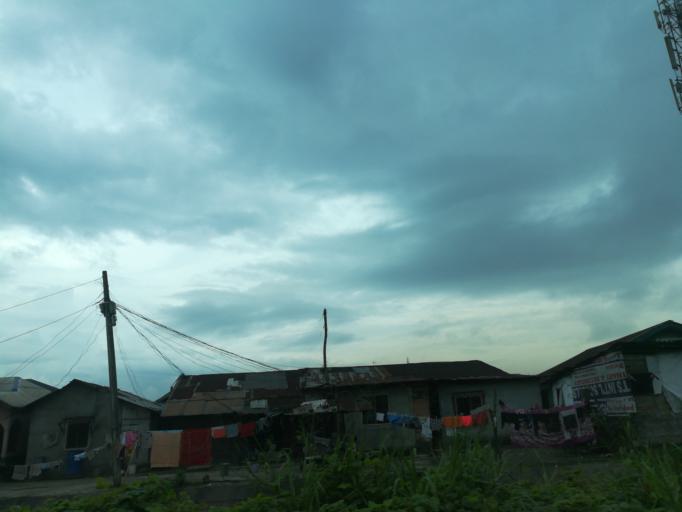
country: NG
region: Rivers
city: Port Harcourt
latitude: 4.8159
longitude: 7.0158
